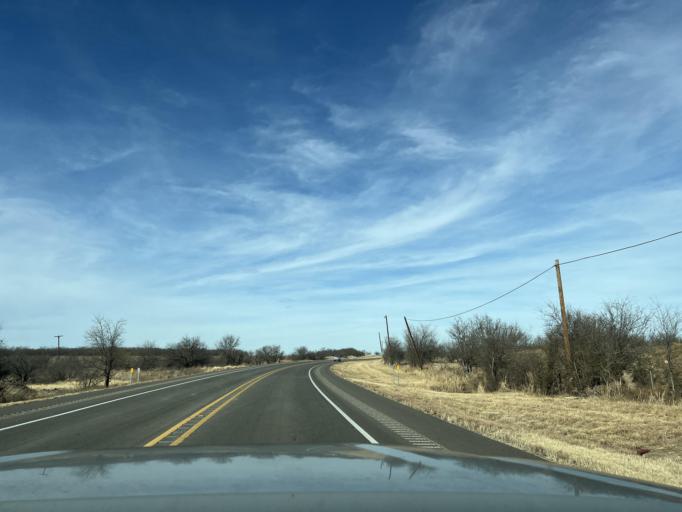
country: US
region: Texas
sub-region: Shackelford County
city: Albany
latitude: 32.5809
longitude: -99.1837
